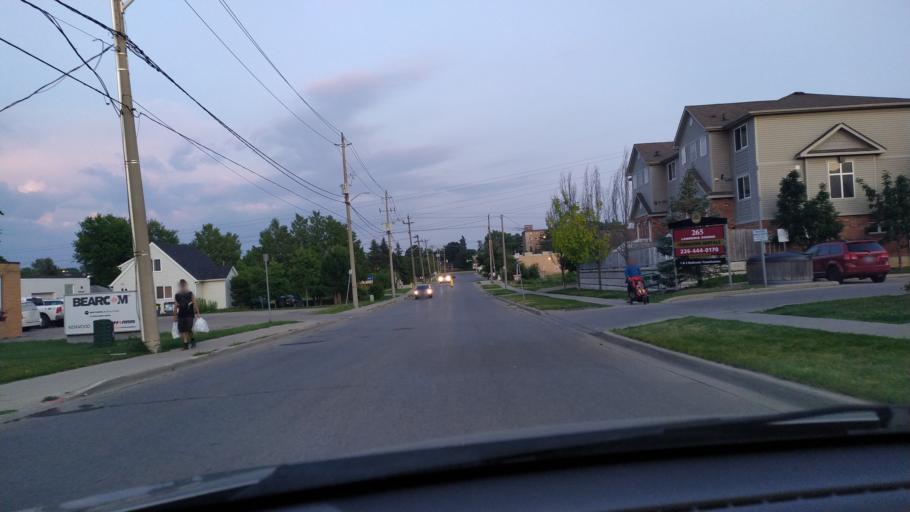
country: CA
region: Ontario
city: Kitchener
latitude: 43.4404
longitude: -80.5126
